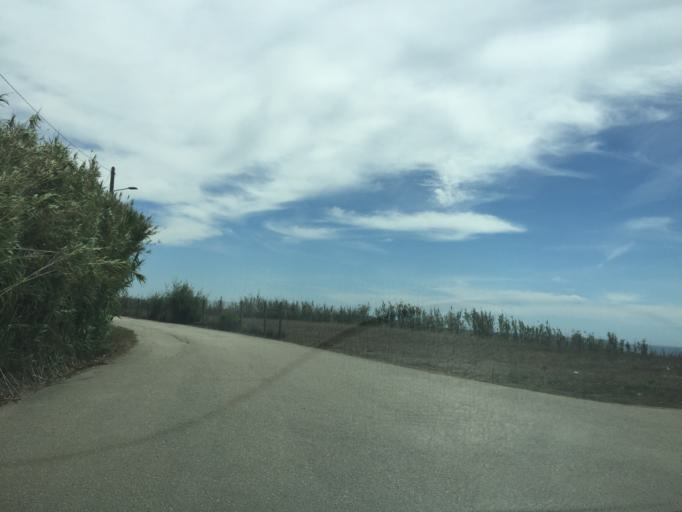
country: PT
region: Lisbon
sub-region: Lourinha
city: Lourinha
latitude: 39.2067
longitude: -9.3408
